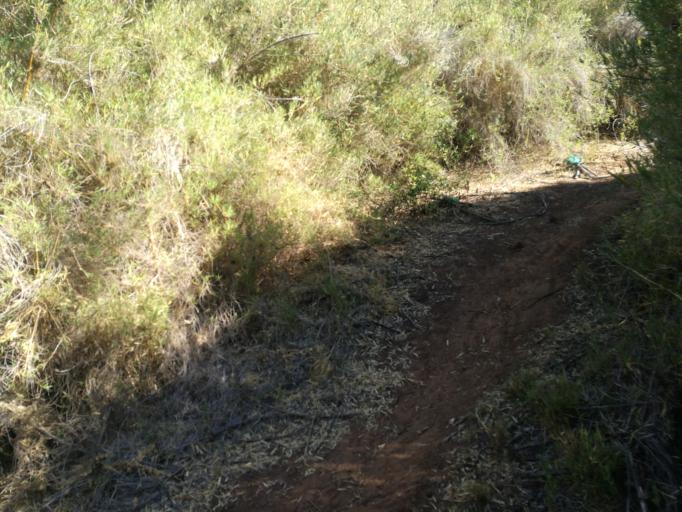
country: CL
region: Valparaiso
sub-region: Provincia de Valparaiso
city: Valparaiso
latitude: -33.0781
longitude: -71.6443
